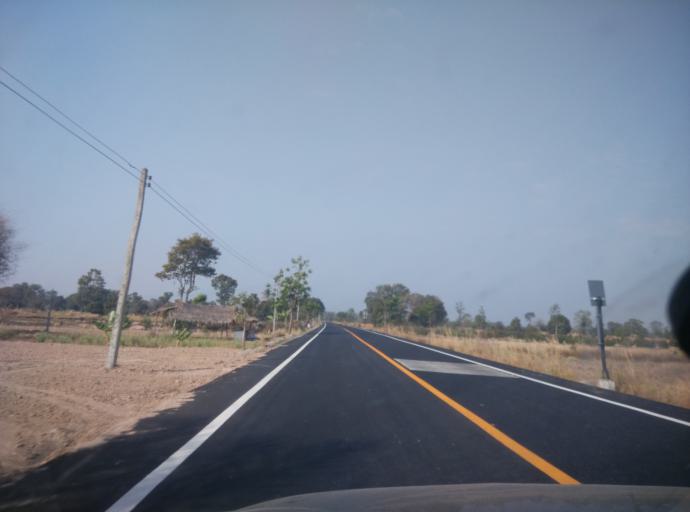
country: TH
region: Sisaket
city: Si Sa Ket
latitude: 15.1236
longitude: 104.2452
